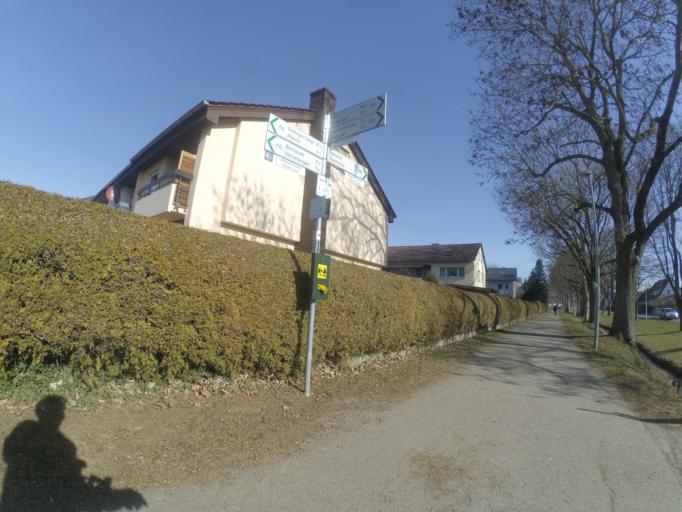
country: DE
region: Baden-Wuerttemberg
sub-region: Tuebingen Region
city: Langenau
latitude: 48.4918
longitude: 10.1146
